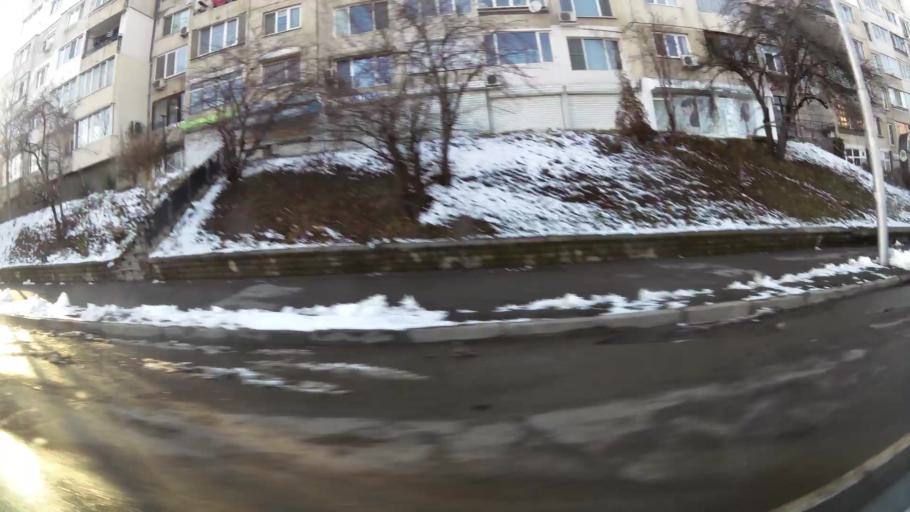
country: BG
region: Sofia-Capital
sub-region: Stolichna Obshtina
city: Sofia
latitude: 42.6793
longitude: 23.3710
